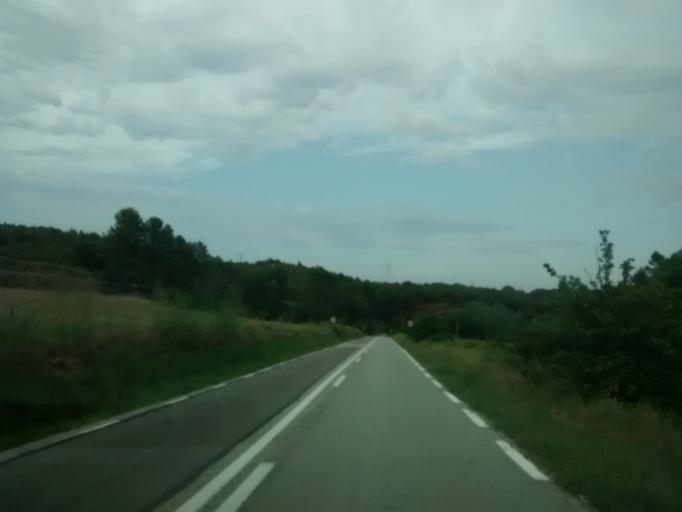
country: ES
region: Catalonia
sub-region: Provincia de Barcelona
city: Rajadell
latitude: 41.7631
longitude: 1.7240
